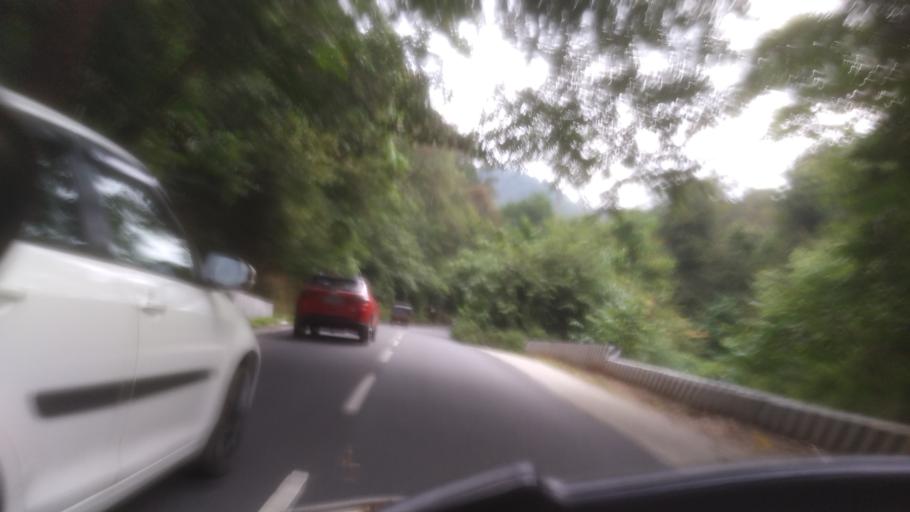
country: IN
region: Kerala
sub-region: Idukki
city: Kuttampuzha
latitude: 10.0652
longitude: 76.8044
